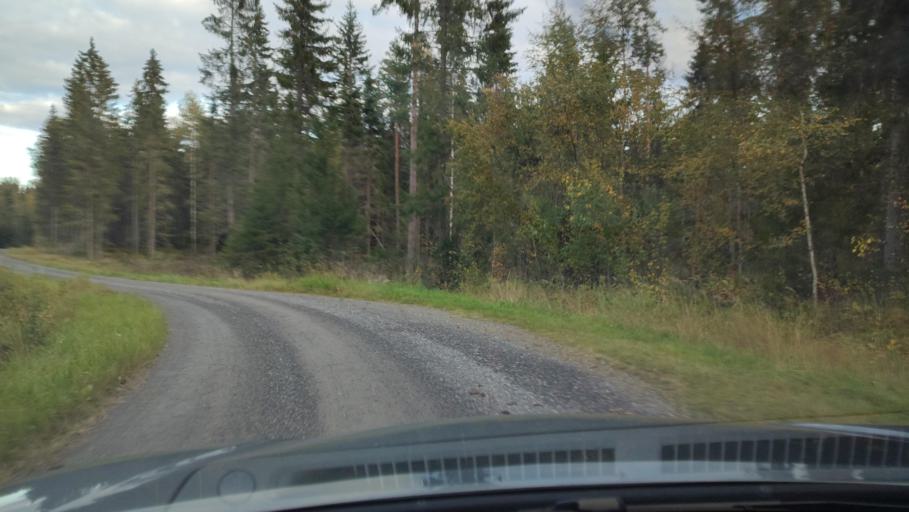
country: FI
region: Ostrobothnia
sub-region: Sydosterbotten
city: Kristinestad
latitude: 62.2323
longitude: 21.4064
